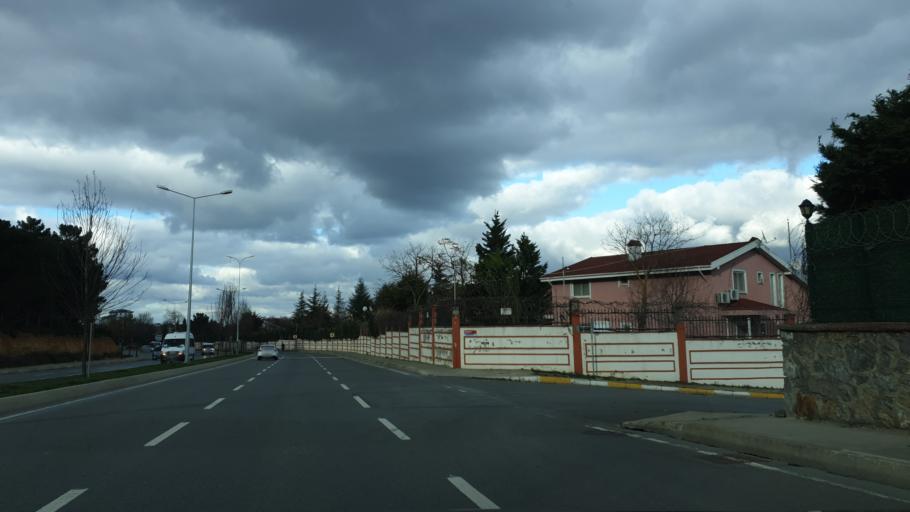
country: TR
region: Istanbul
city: Sultanbeyli
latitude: 40.9281
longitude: 29.2723
